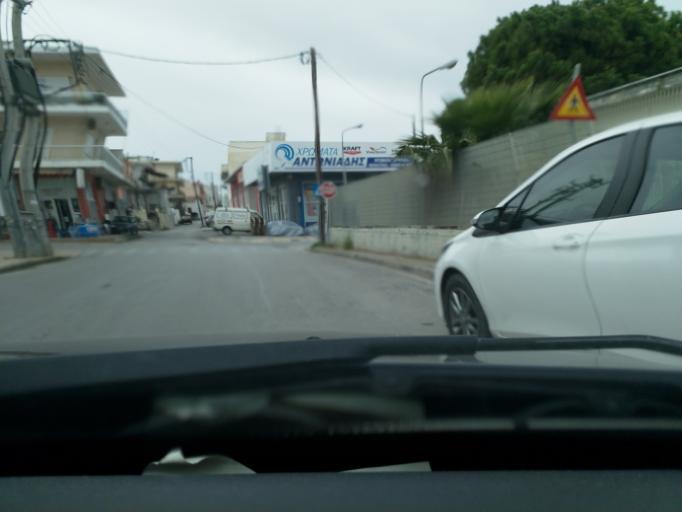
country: GR
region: Crete
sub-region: Nomos Chanias
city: Chania
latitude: 35.5010
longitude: 24.0219
